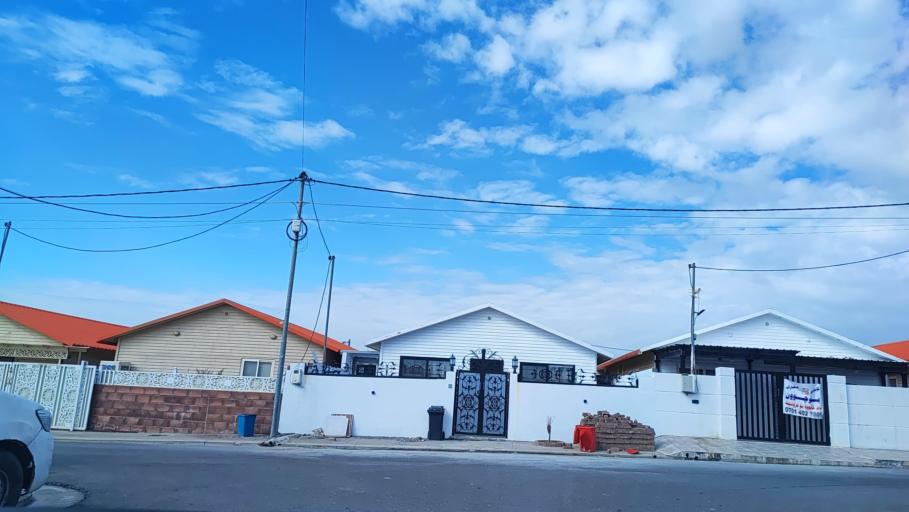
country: IQ
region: Arbil
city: Erbil
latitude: 36.2846
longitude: 44.0689
